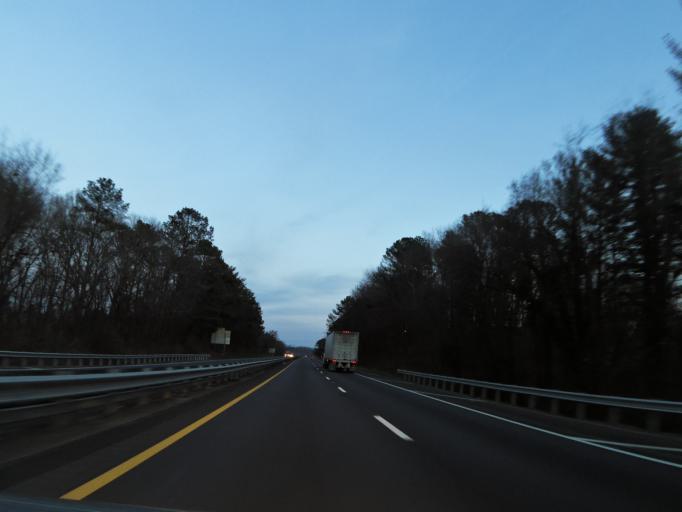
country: US
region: Tennessee
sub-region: Roane County
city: Kingston
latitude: 35.8883
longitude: -84.5223
